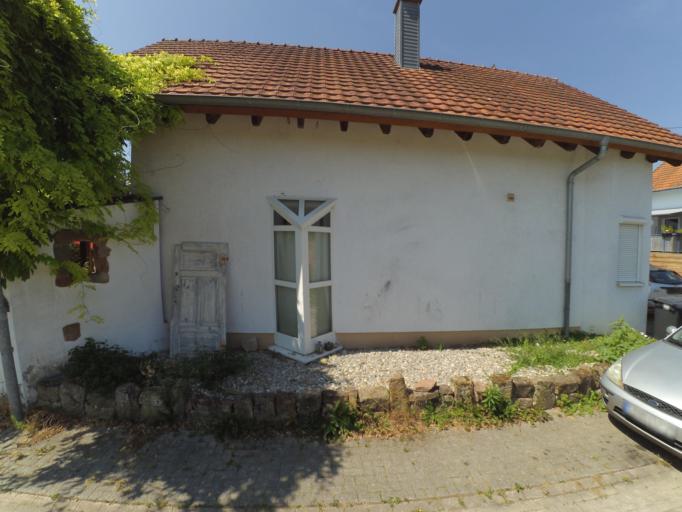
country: DE
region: Rheinland-Pfalz
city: Bornheim
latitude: 49.2220
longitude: 8.1724
